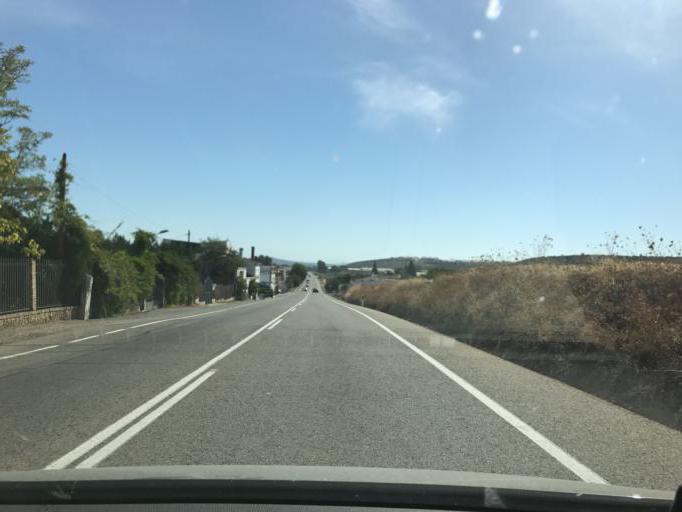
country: ES
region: Andalusia
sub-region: Province of Cordoba
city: Castro del Rio
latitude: 37.6845
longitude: -4.4843
